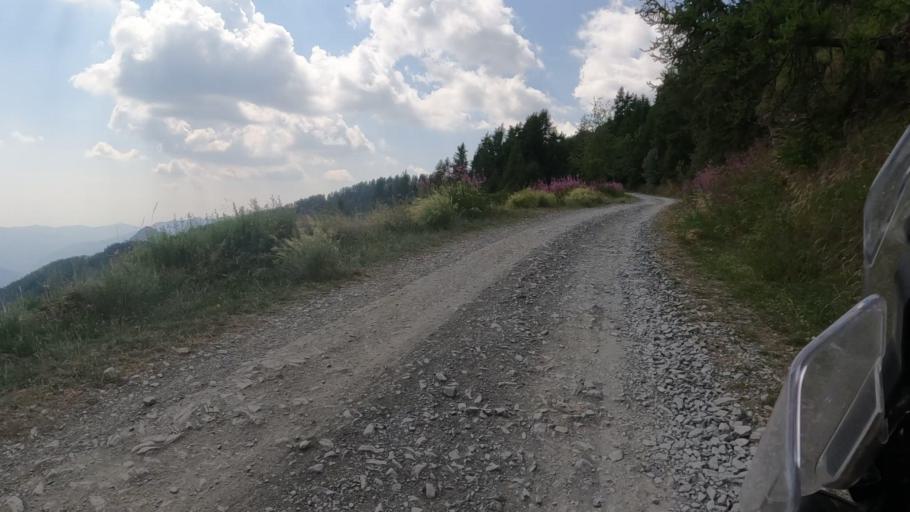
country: FR
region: Provence-Alpes-Cote d'Azur
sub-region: Departement des Alpes-Maritimes
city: Tende
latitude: 44.0267
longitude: 7.6641
